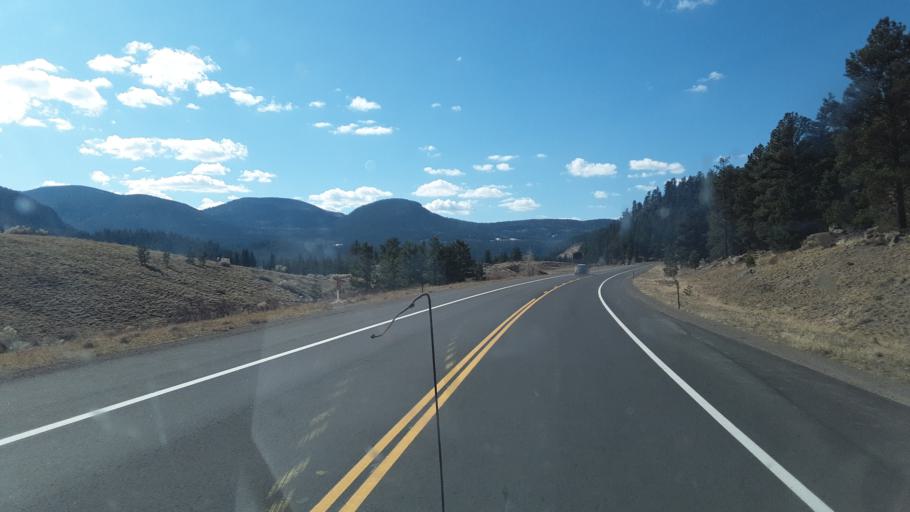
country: US
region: Colorado
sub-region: Rio Grande County
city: Del Norte
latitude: 37.6389
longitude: -106.6680
